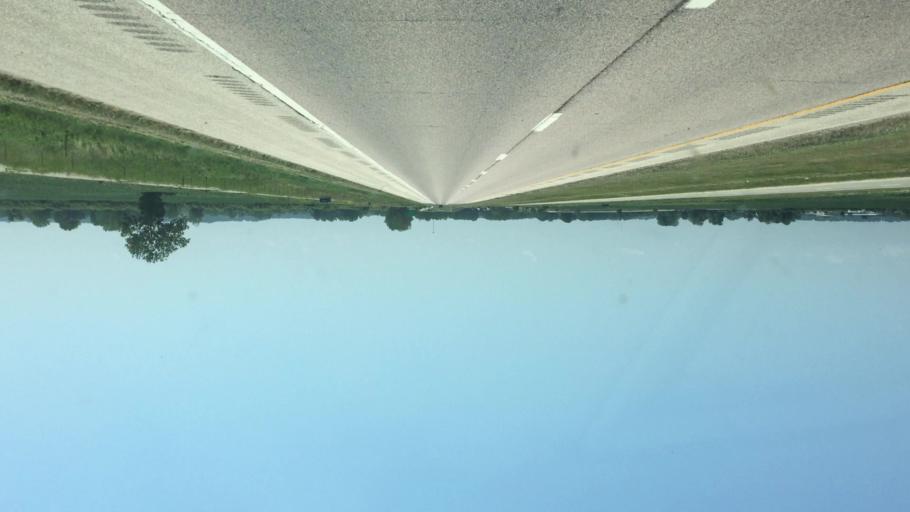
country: US
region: Kansas
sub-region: Doniphan County
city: Elwood
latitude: 39.7403
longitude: -94.9101
